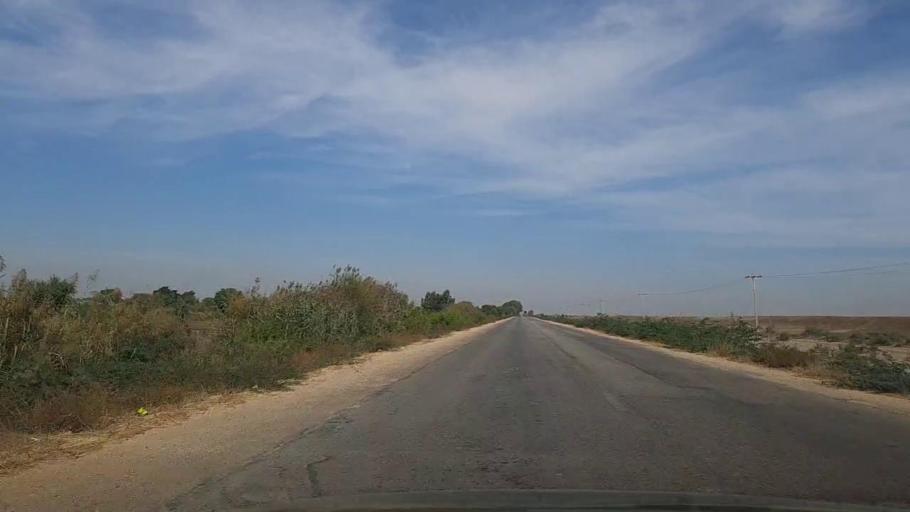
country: PK
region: Sindh
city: Daro Mehar
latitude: 24.9515
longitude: 68.1135
